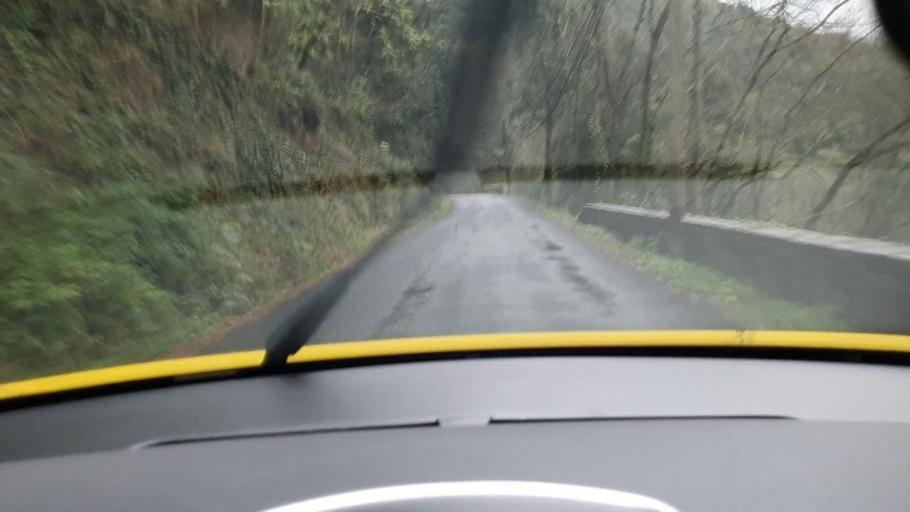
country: FR
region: Languedoc-Roussillon
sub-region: Departement du Gard
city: Sumene
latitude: 43.9884
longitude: 3.7136
